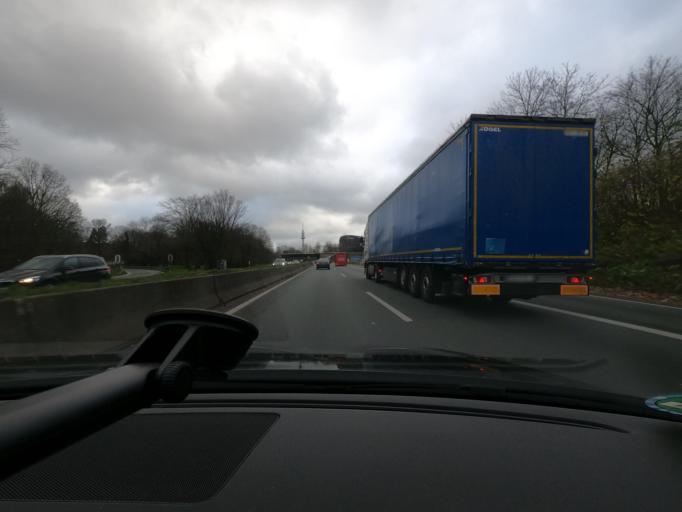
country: DE
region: North Rhine-Westphalia
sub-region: Regierungsbezirk Arnsberg
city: Bochum
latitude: 51.4962
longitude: 7.2299
